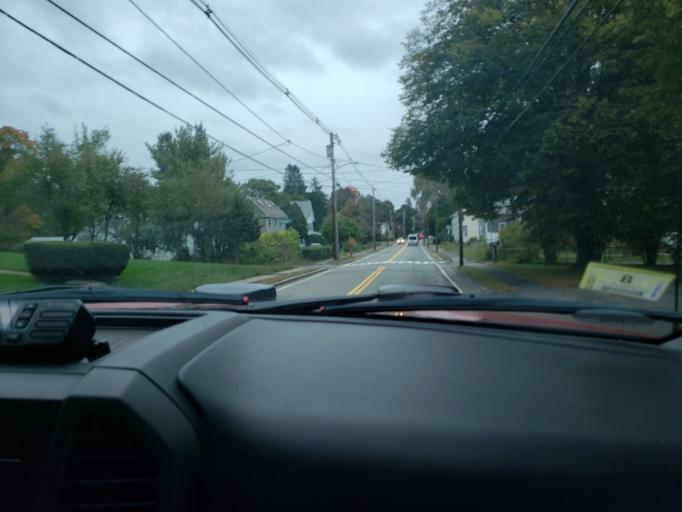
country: US
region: Massachusetts
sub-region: Middlesex County
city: Natick
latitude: 42.2743
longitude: -71.3527
